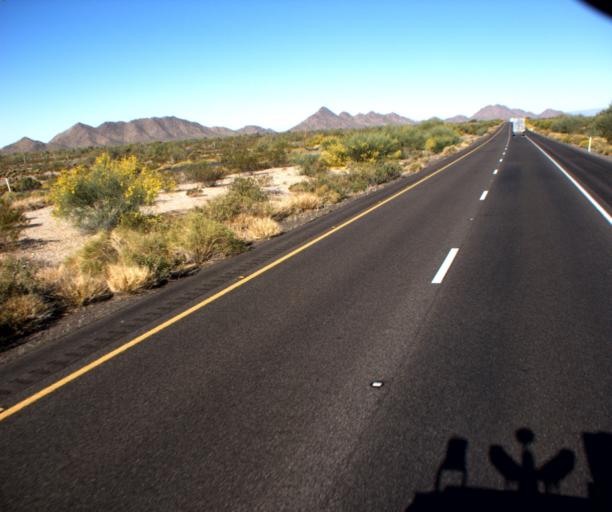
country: US
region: Arizona
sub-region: Maricopa County
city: Gila Bend
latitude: 32.8853
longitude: -112.4675
